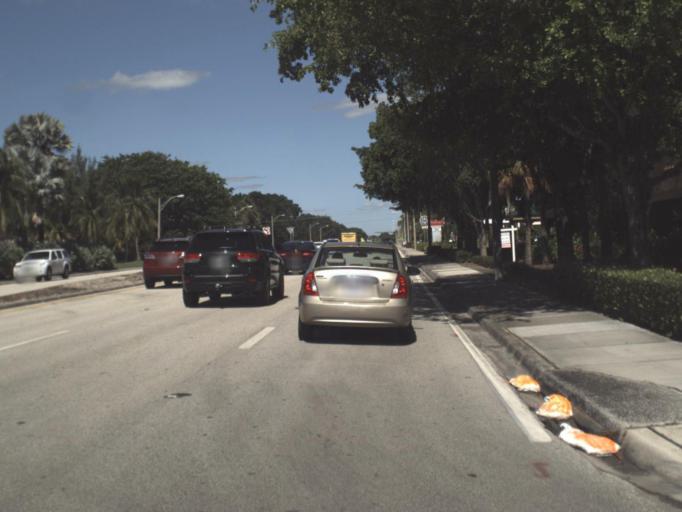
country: US
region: Florida
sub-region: Collier County
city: Naples
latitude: 26.1600
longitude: -81.7975
